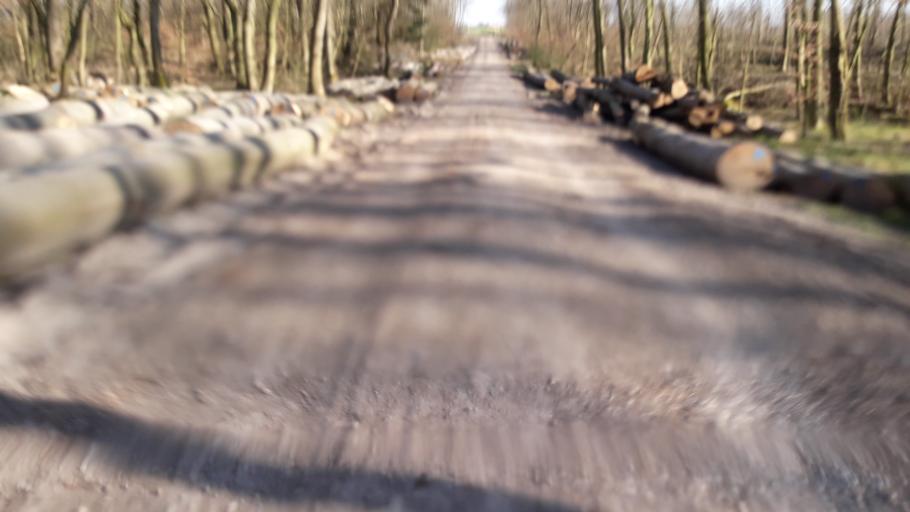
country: DE
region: North Rhine-Westphalia
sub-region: Regierungsbezirk Detmold
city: Salzkotten
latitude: 51.6609
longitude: 8.6698
